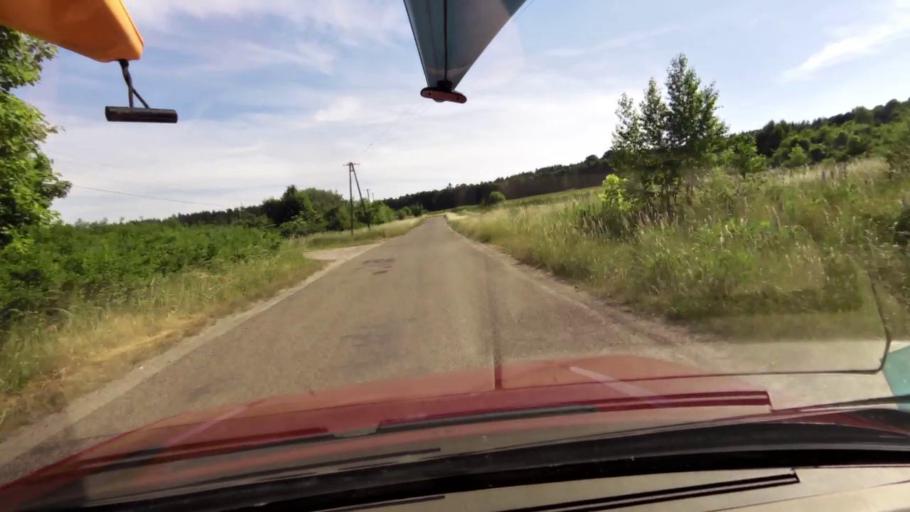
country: PL
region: Pomeranian Voivodeship
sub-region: Powiat slupski
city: Kepice
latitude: 54.1745
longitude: 16.8870
